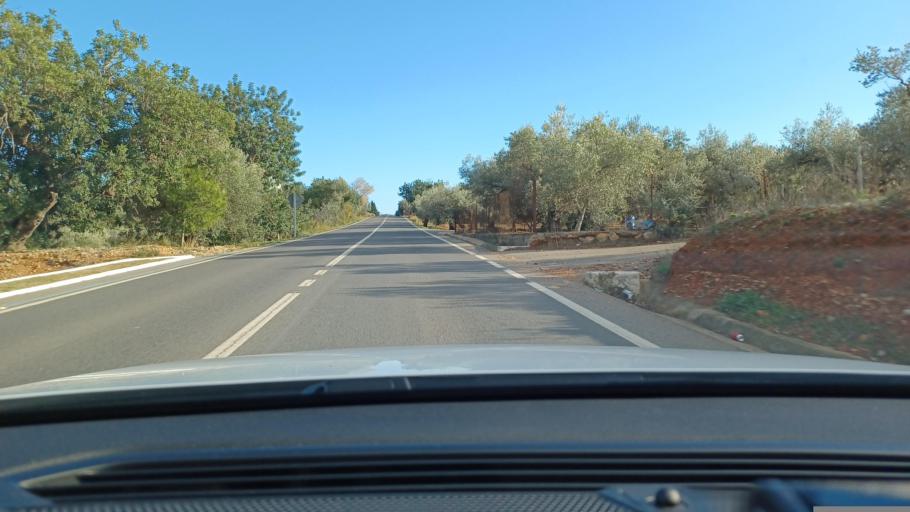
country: ES
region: Catalonia
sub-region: Provincia de Tarragona
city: Masdenverge
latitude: 40.7112
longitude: 0.5358
